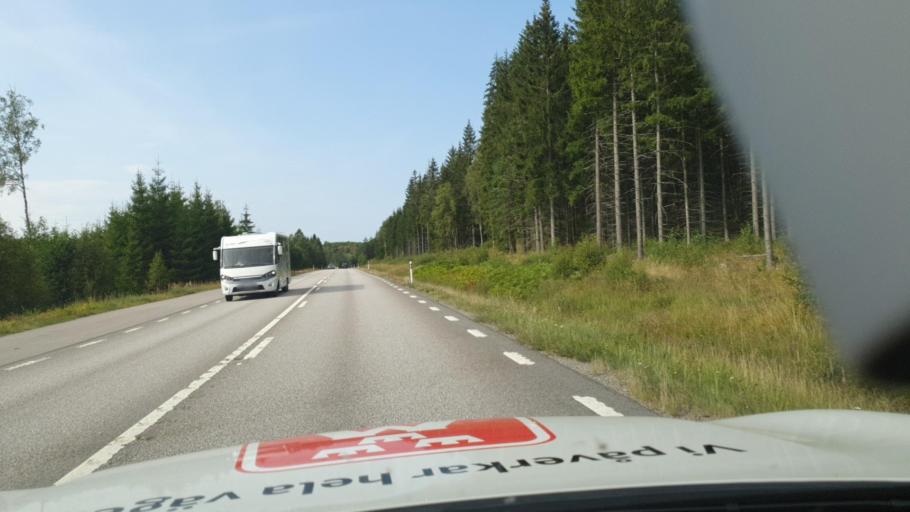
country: SE
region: Vaestra Goetaland
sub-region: Dals-Ed Kommun
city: Ed
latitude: 58.8798
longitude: 11.7996
